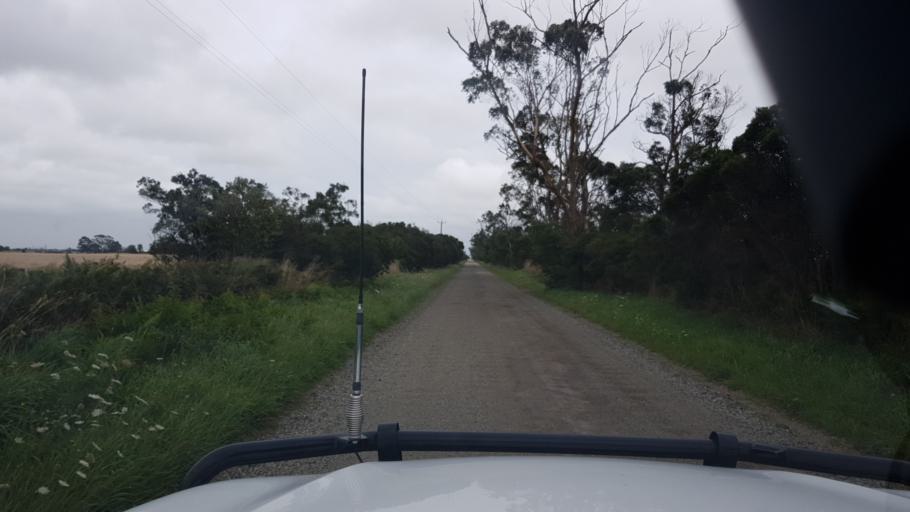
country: AU
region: Victoria
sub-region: Cardinia
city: Bunyip
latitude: -38.1603
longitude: 145.7163
